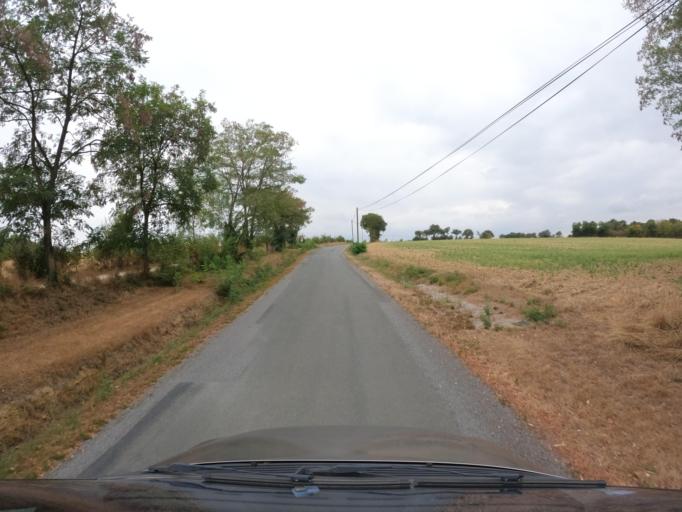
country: FR
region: Pays de la Loire
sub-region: Departement de la Vendee
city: La Guyonniere
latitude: 46.9669
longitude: -1.2612
